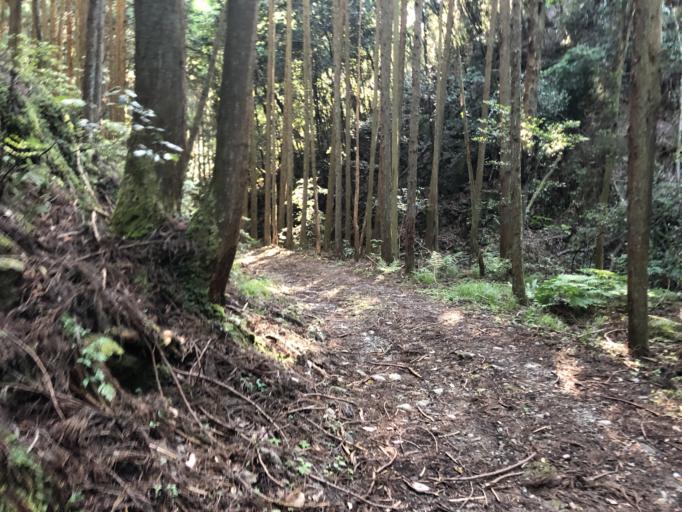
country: JP
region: Kyoto
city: Kameoka
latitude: 34.9867
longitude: 135.6252
